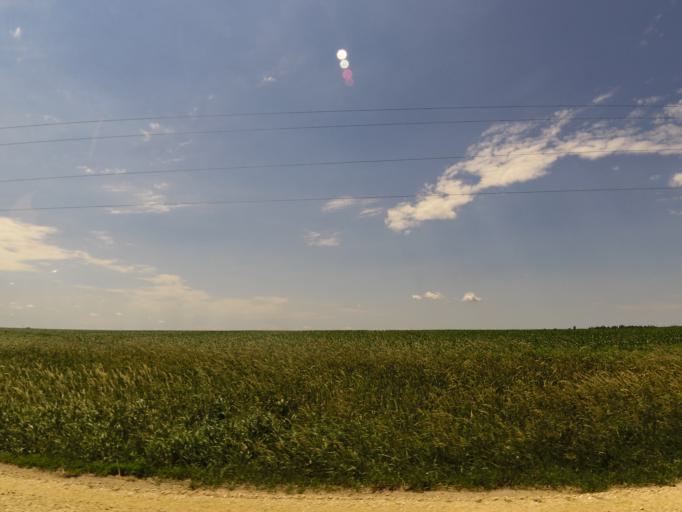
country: US
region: Iowa
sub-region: Bremer County
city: Tripoli
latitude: 42.7150
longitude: -92.2519
